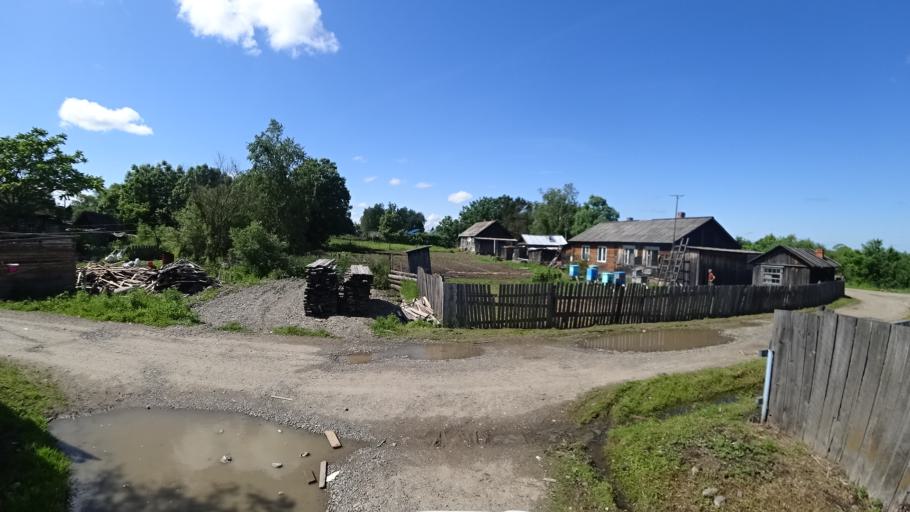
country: RU
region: Khabarovsk Krai
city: Khor
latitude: 47.8858
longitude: 135.0366
